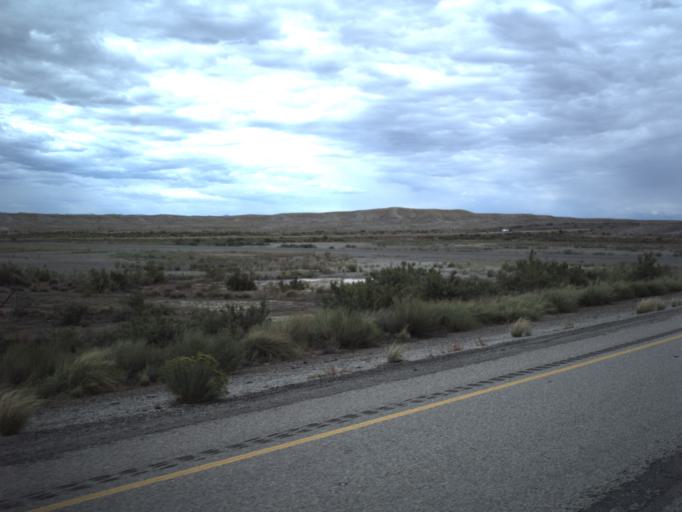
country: US
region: Utah
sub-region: Grand County
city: Moab
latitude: 38.9754
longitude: -109.3514
